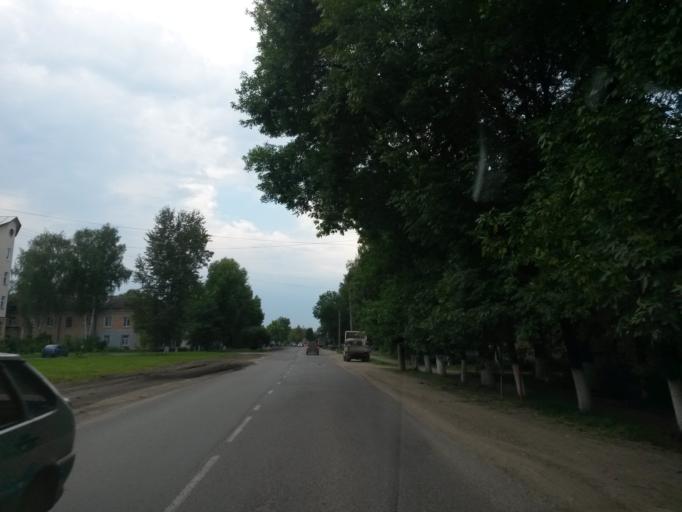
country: RU
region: Jaroslavl
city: Yaroslavl
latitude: 57.6059
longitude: 39.8153
